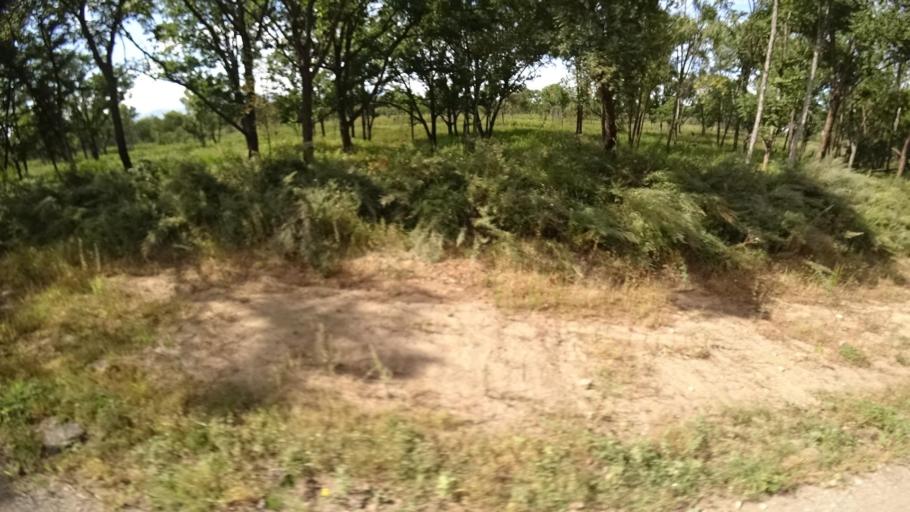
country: RU
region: Primorskiy
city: Yakovlevka
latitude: 44.3975
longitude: 133.5613
